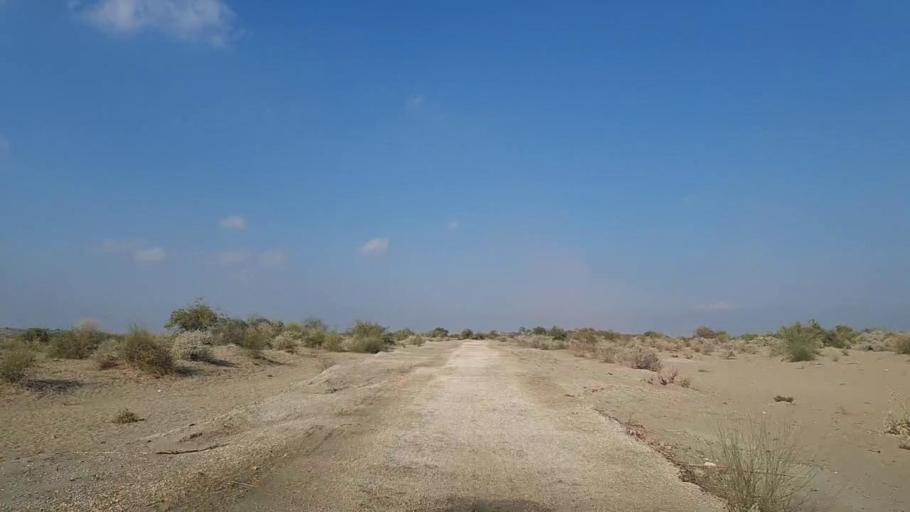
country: PK
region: Sindh
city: Tando Mittha Khan
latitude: 26.0227
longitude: 69.2511
